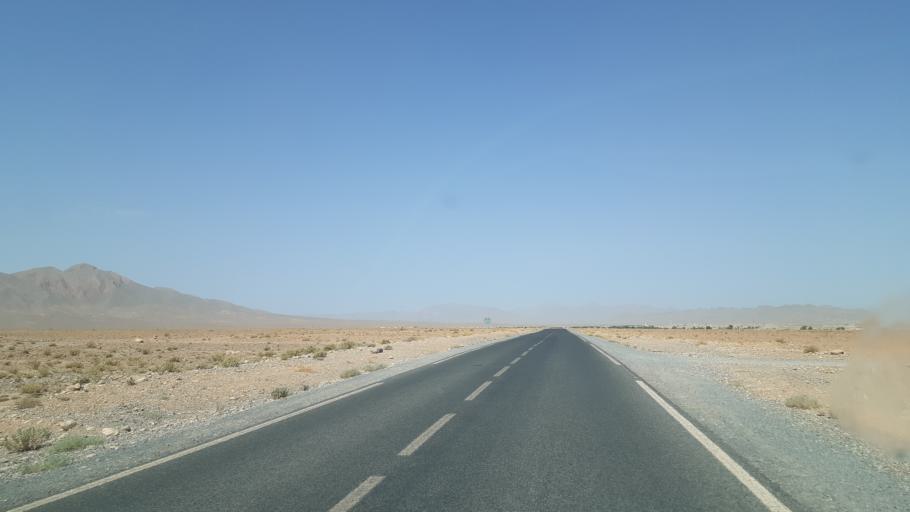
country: MA
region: Meknes-Tafilalet
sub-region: Errachidia
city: Amouguer
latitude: 32.2306
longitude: -4.6513
